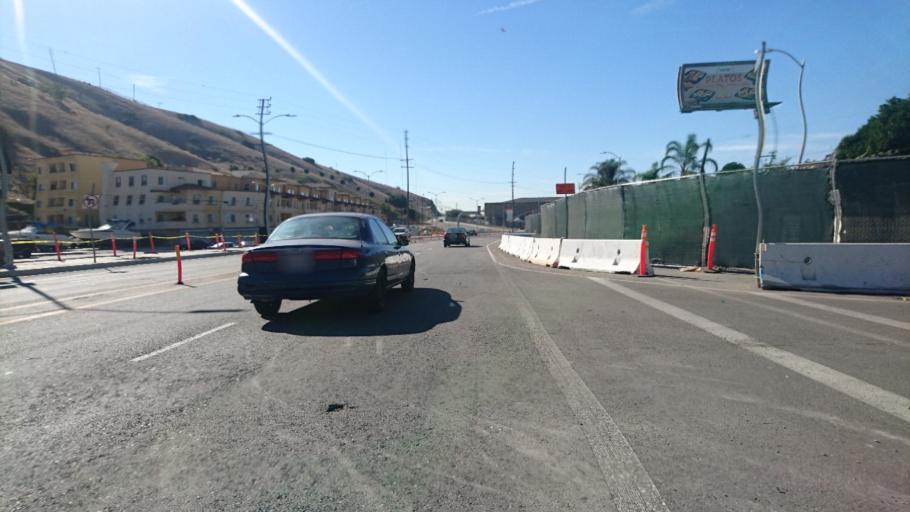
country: US
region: California
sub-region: Los Angeles County
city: Belvedere
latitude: 34.0791
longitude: -118.1934
